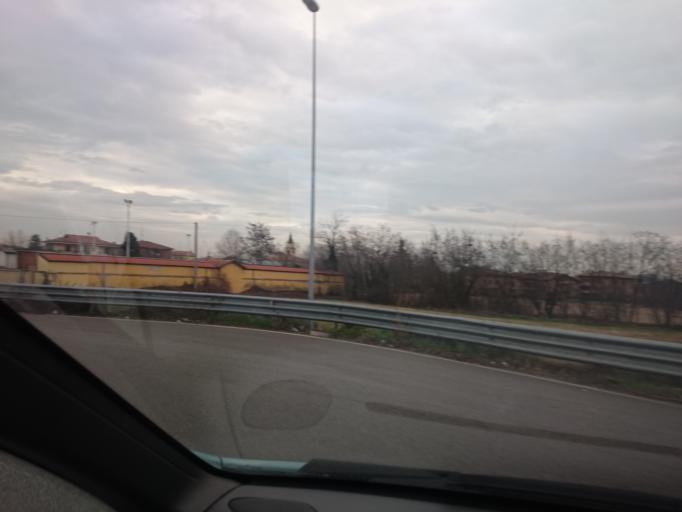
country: IT
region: Emilia-Romagna
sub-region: Provincia di Reggio Emilia
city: Scandiano
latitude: 44.5939
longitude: 10.7036
